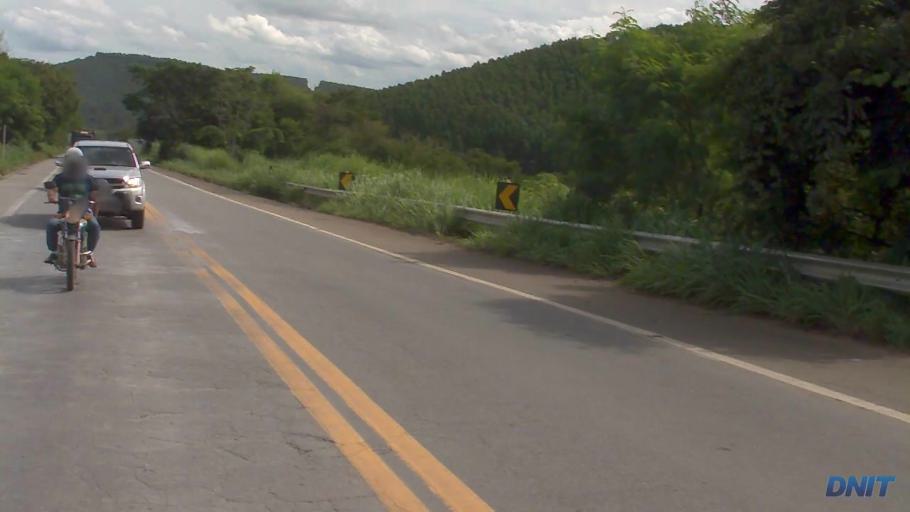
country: BR
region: Minas Gerais
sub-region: Ipaba
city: Ipaba
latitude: -19.3365
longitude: -42.4254
